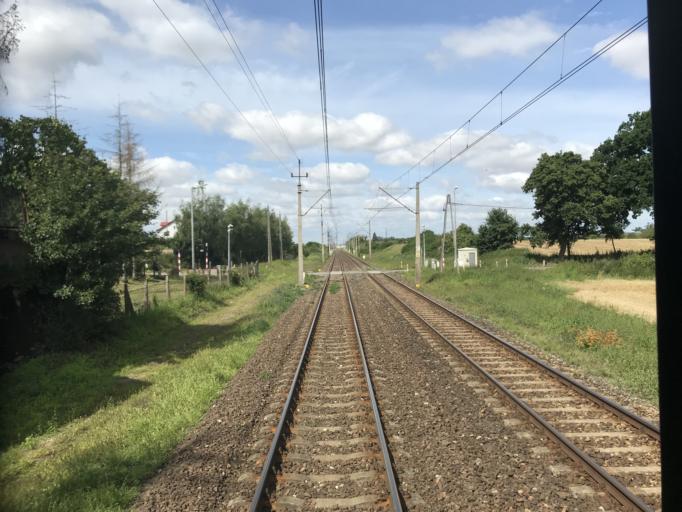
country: PL
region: Pomeranian Voivodeship
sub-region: Powiat malborski
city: Malbork
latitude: 54.0336
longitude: 19.0842
